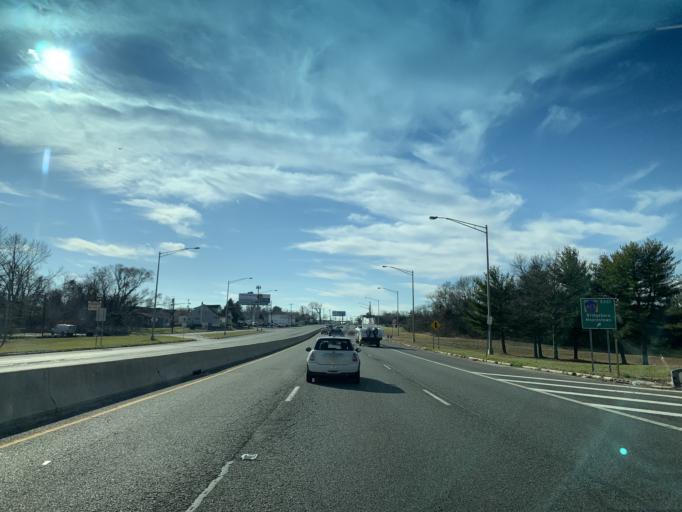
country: US
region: New Jersey
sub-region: Burlington County
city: Delanco
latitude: 40.0264
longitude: -74.9355
